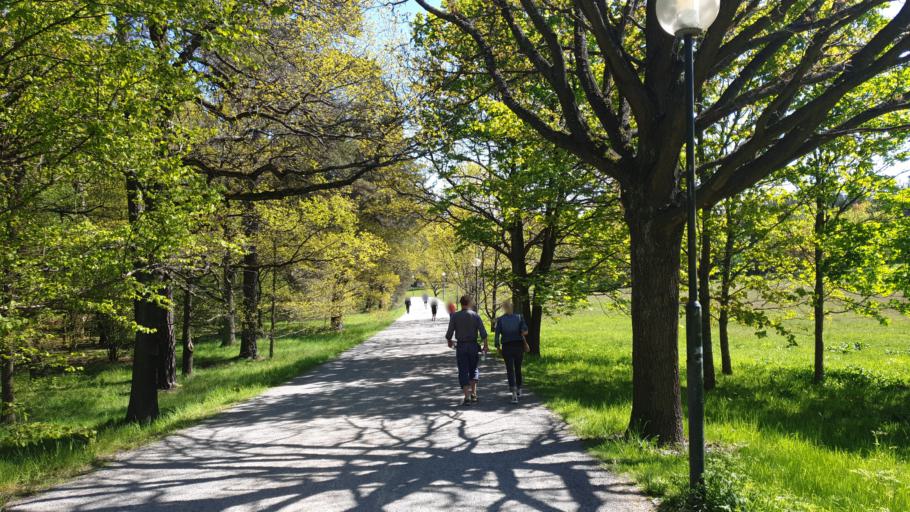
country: SE
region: Stockholm
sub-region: Norrtalje Kommun
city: Bergshamra
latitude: 59.3596
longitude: 18.0326
